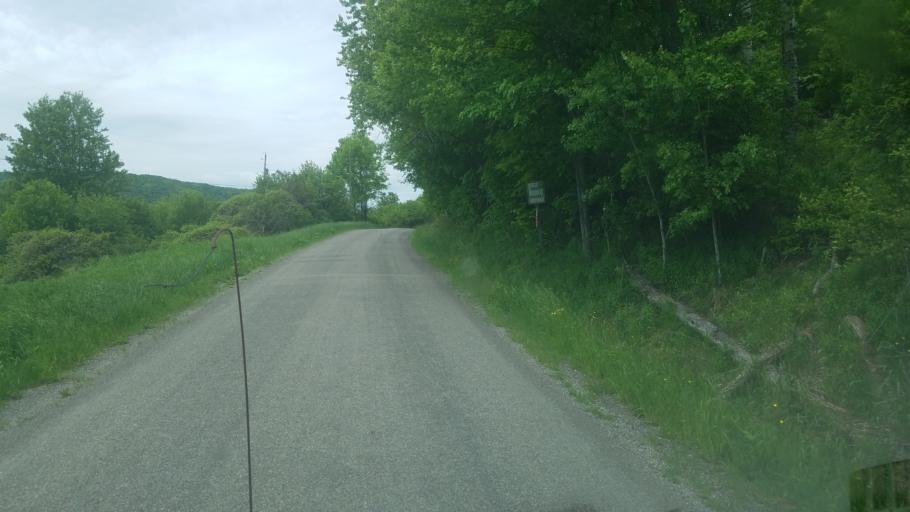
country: US
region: Pennsylvania
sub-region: Tioga County
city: Westfield
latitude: 41.8906
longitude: -77.6000
